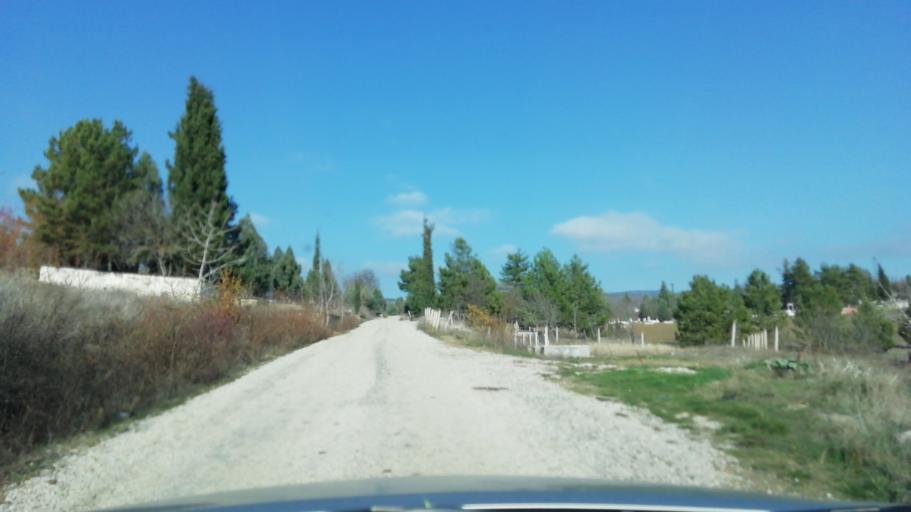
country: TR
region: Karabuk
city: Safranbolu
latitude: 41.2291
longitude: 32.7765
